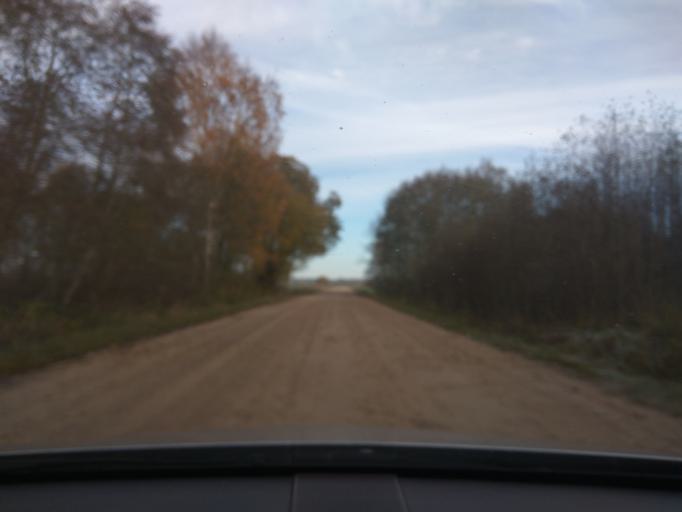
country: LV
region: Aizpute
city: Aizpute
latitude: 56.8489
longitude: 21.6640
